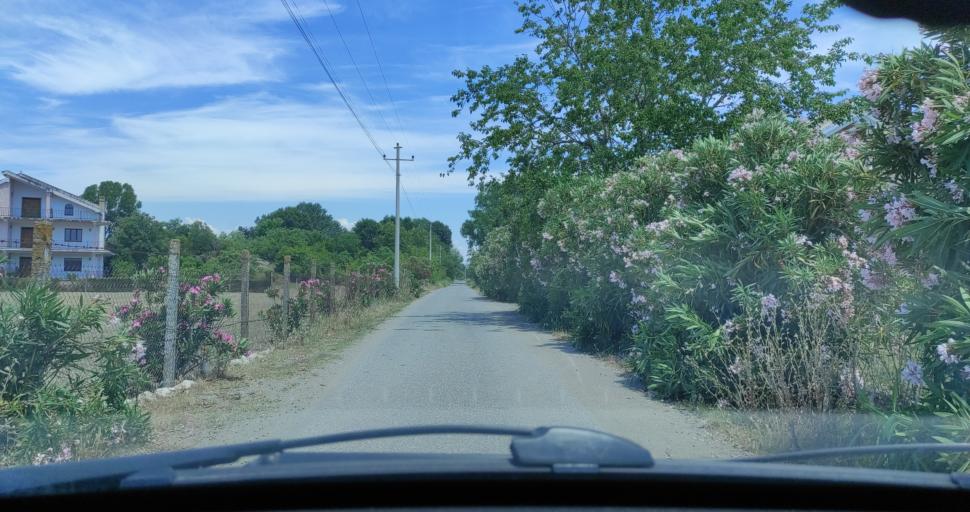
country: AL
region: Shkoder
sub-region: Rrethi i Shkodres
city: Velipoje
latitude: 41.8745
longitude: 19.3808
